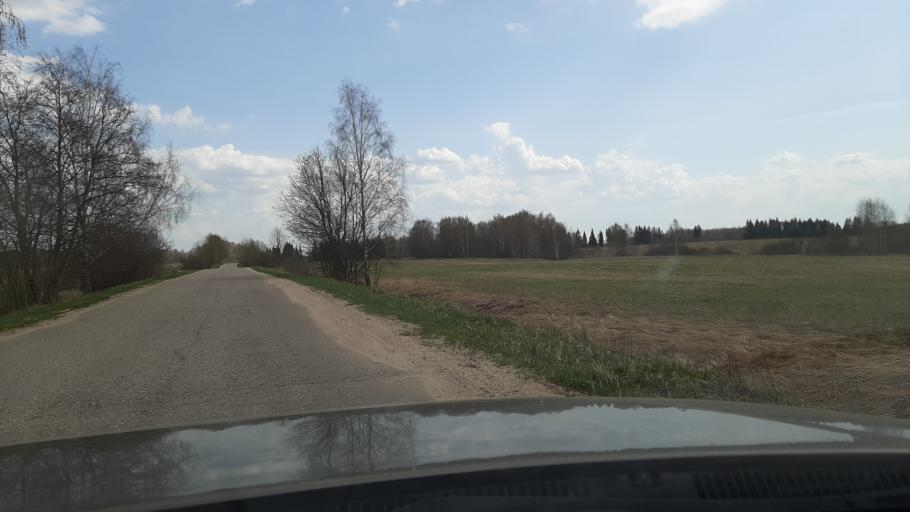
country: RU
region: Ivanovo
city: Furmanov
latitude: 57.2974
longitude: 41.1709
